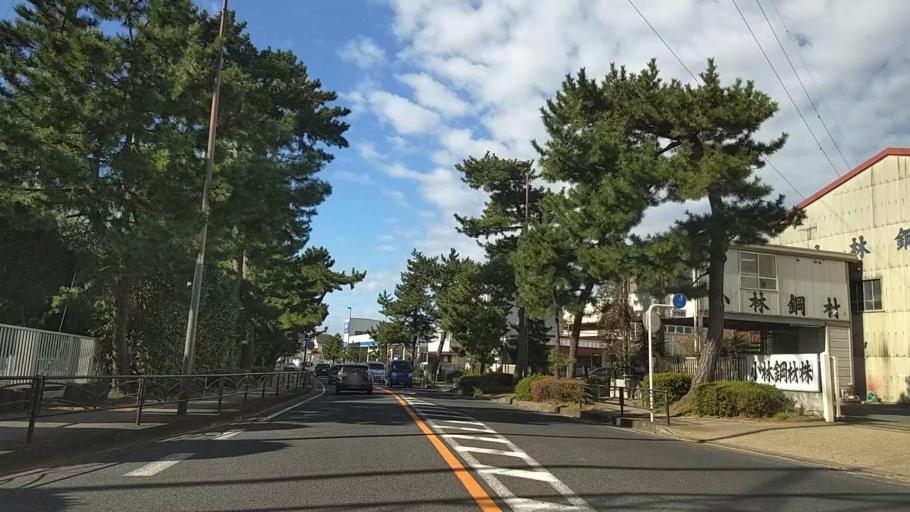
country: JP
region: Kanagawa
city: Chigasaki
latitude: 35.3376
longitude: 139.4220
